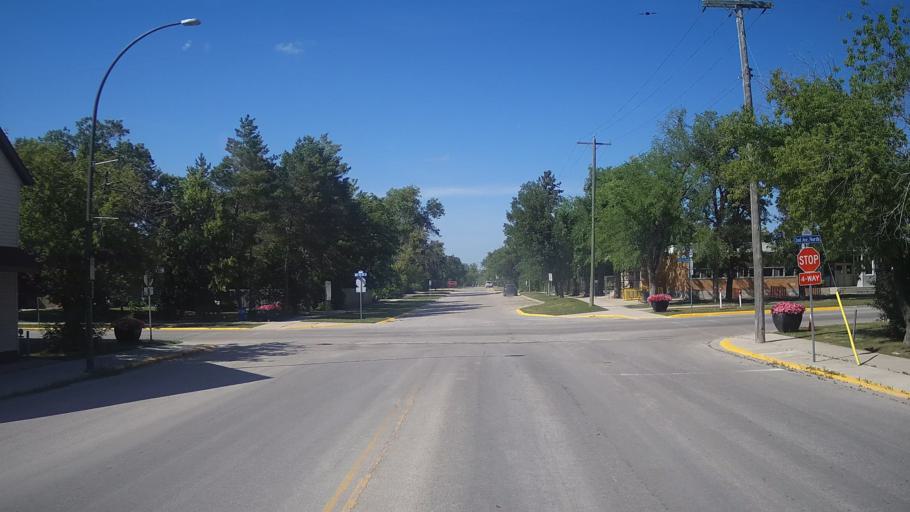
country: CA
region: Manitoba
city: Stonewall
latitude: 50.1373
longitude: -97.3266
